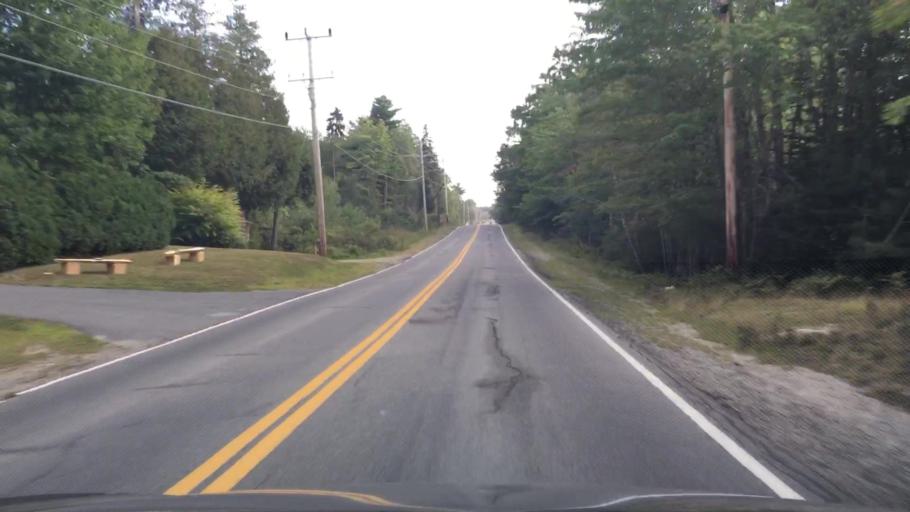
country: US
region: Maine
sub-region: Hancock County
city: Surry
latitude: 44.4357
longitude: -68.5723
